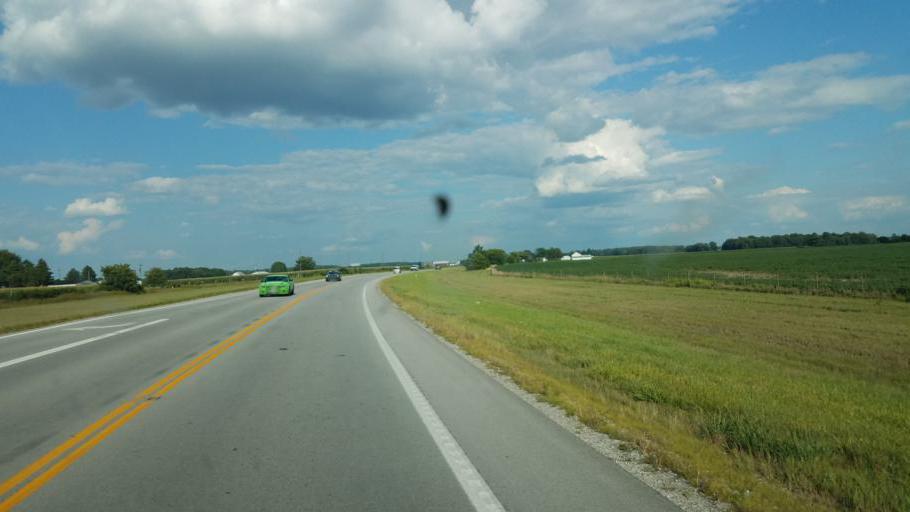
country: US
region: Ohio
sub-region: Wood County
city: Bowling Green
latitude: 41.3617
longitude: -83.5657
